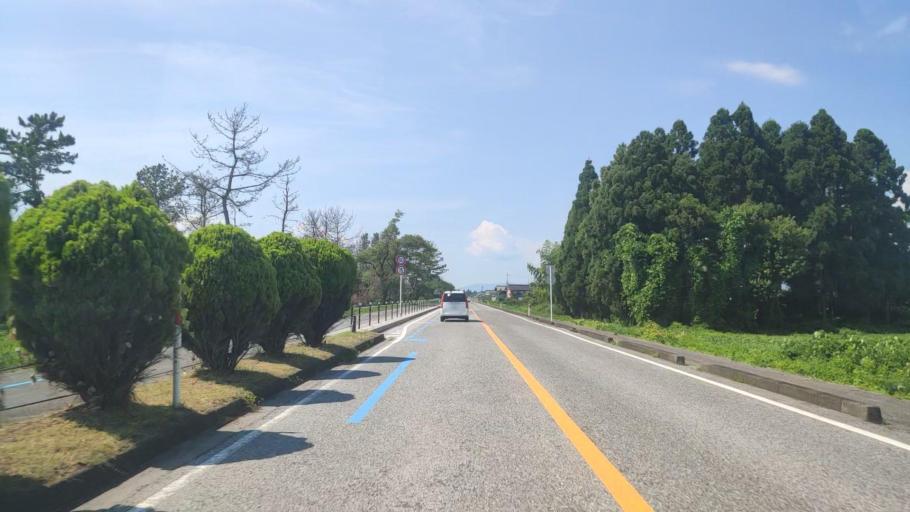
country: JP
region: Shiga Prefecture
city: Nagahama
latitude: 35.3985
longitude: 136.2174
